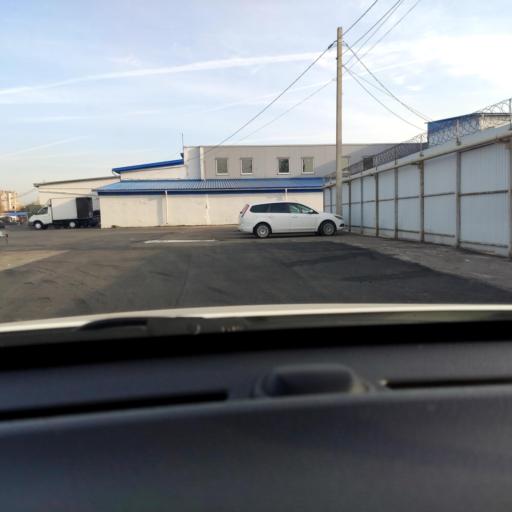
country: RU
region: Voronezj
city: Voronezh
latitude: 51.6558
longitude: 39.2839
